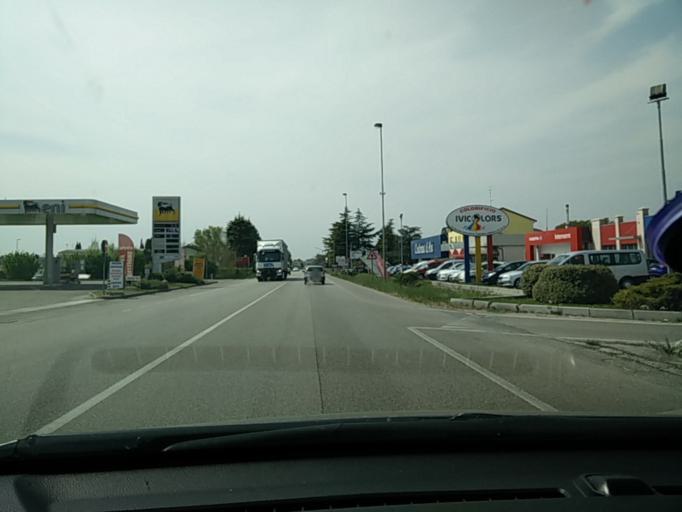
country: IT
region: Friuli Venezia Giulia
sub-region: Provincia di Pordenone
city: Pordenone
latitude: 45.9725
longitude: 12.6431
